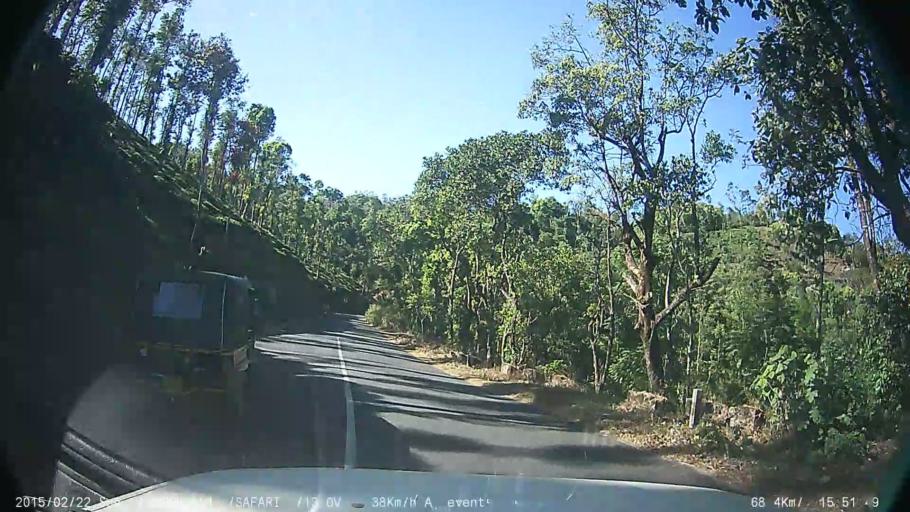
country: IN
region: Kerala
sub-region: Kottayam
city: Erattupetta
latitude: 9.5713
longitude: 77.0087
